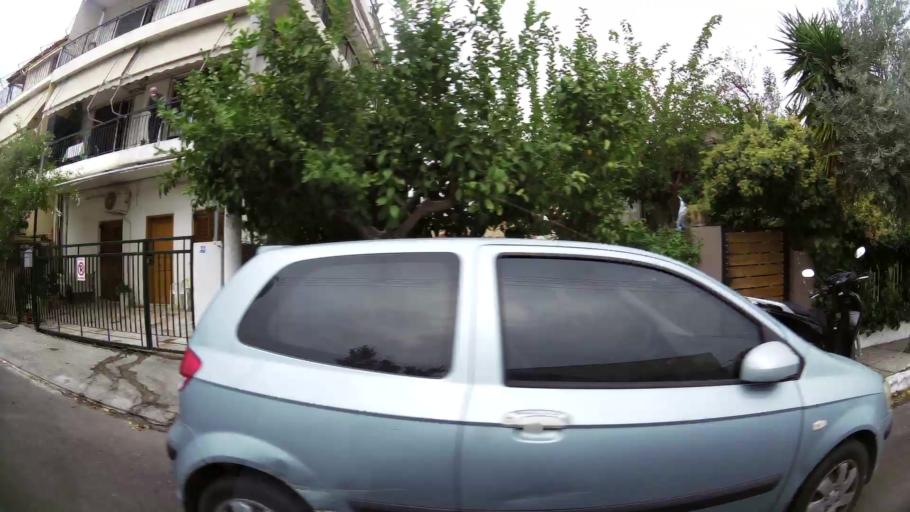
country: GR
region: Attica
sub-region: Nomarchia Athinas
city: Chaidari
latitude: 37.9999
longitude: 23.6658
